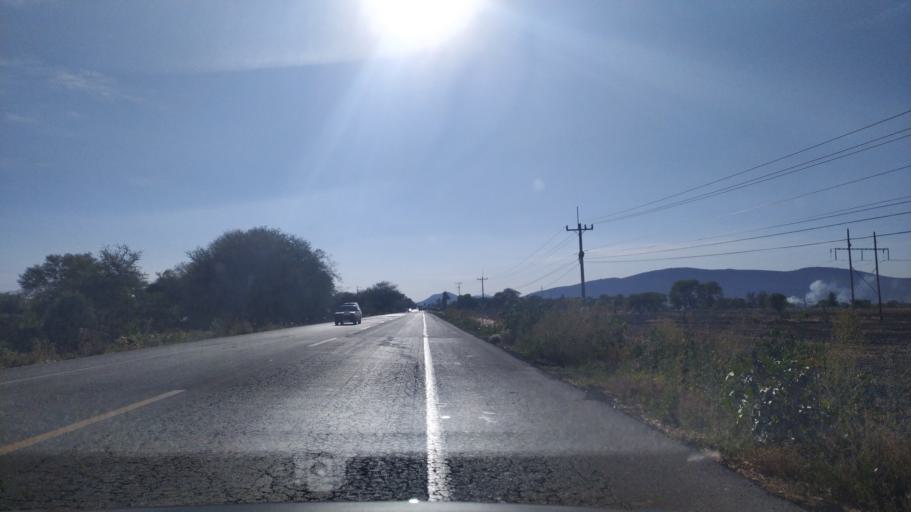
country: MX
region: Michoacan
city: Brisenas
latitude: 20.2932
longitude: -102.6260
